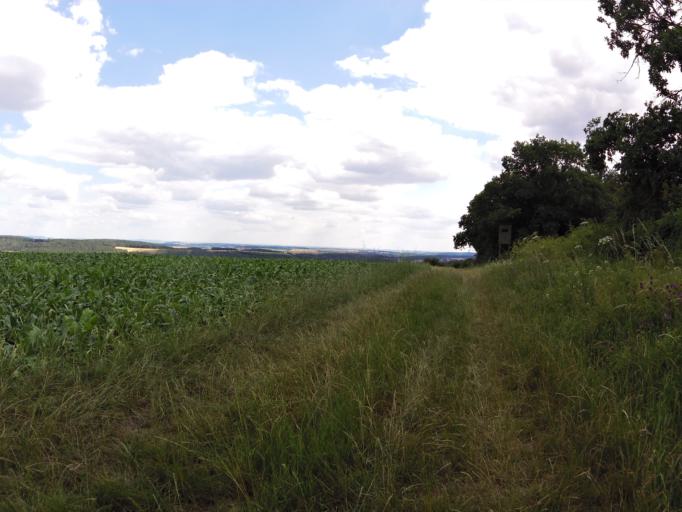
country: DE
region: Bavaria
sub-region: Regierungsbezirk Unterfranken
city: Guntersleben
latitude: 49.8922
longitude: 9.8990
